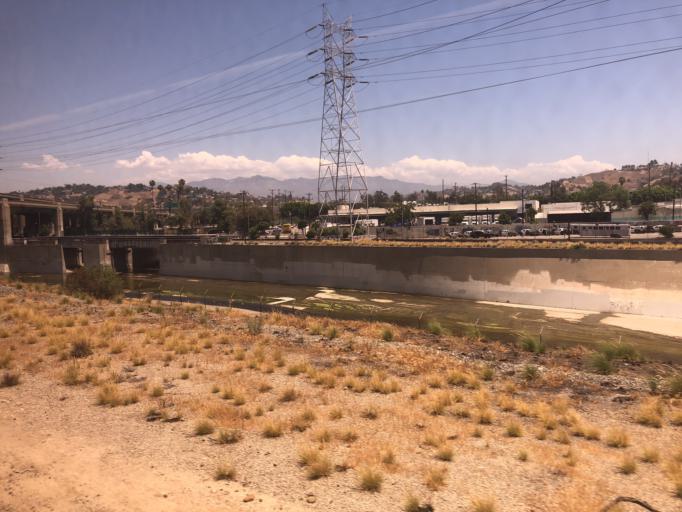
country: US
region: California
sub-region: Los Angeles County
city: Los Angeles
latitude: 34.0777
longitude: -118.2268
